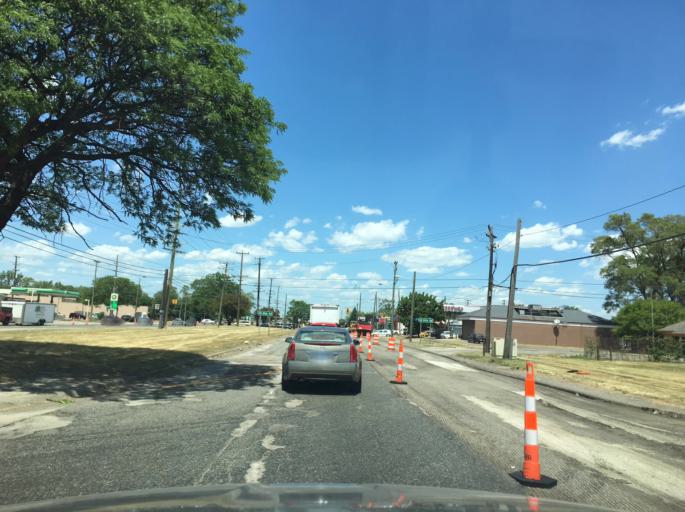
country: US
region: Michigan
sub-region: Macomb County
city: Warren
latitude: 42.4758
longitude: -83.0452
